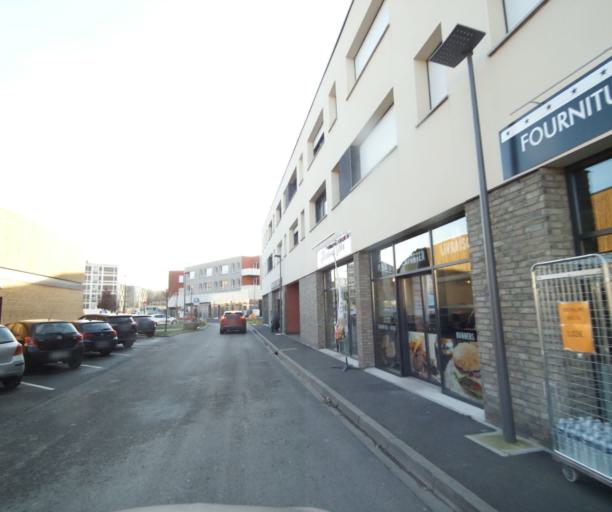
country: FR
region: Nord-Pas-de-Calais
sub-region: Departement du Nord
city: Famars
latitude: 50.3312
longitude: 3.5125
